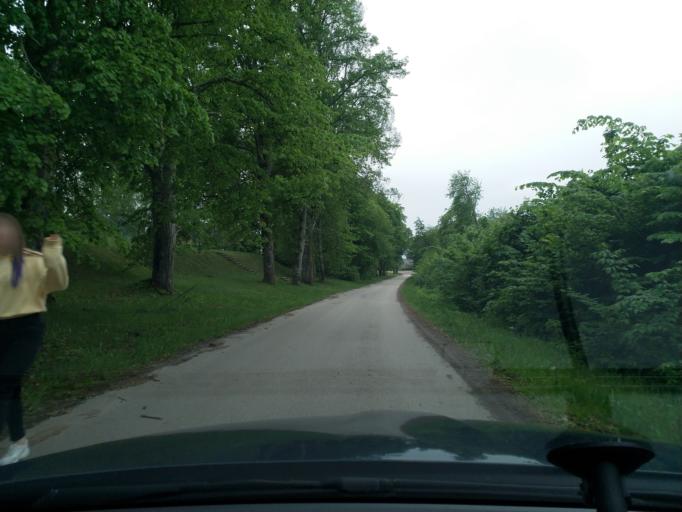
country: LV
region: Kuldigas Rajons
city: Kuldiga
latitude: 56.8812
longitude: 21.8261
